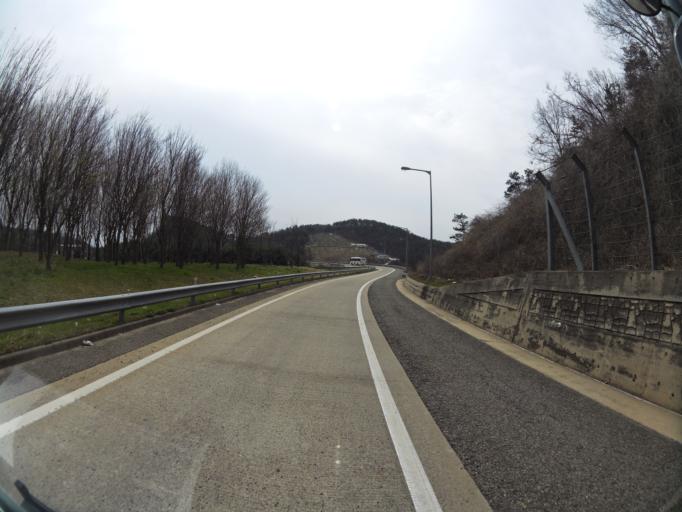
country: KR
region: Gyeongsangnam-do
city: Changnyeong
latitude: 35.4564
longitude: 128.5111
